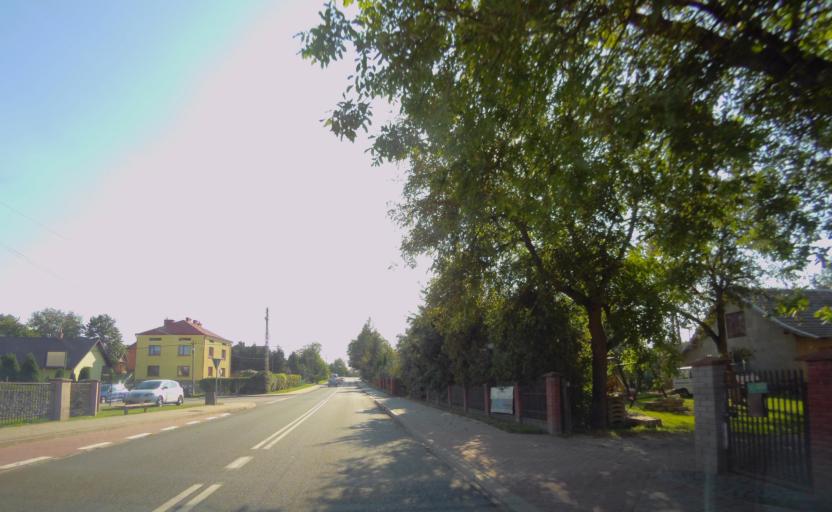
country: PL
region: Subcarpathian Voivodeship
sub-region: Powiat lezajski
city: Stare Miasto
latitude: 50.2901
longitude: 22.4308
